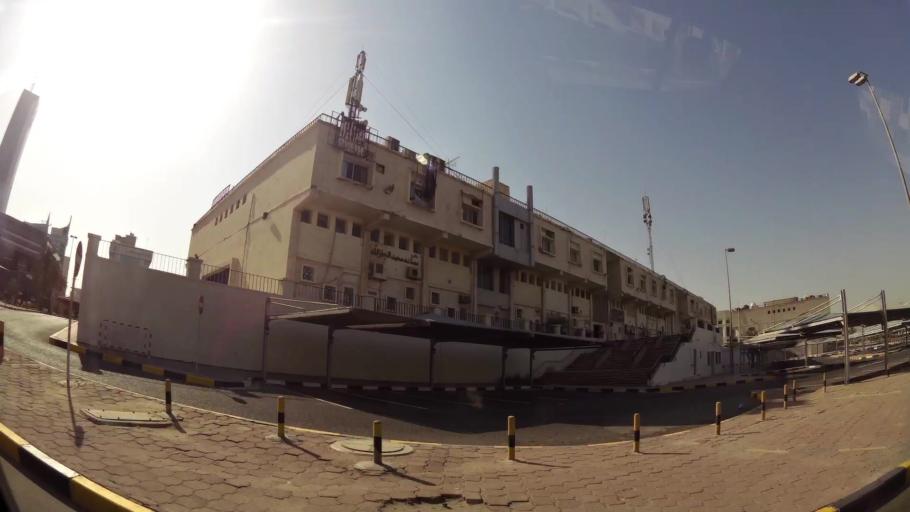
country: KW
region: Al Asimah
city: Kuwait City
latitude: 29.3793
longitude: 47.9735
